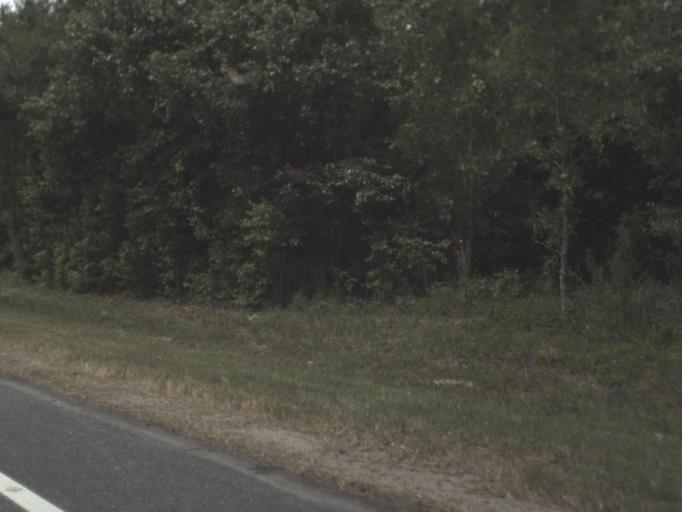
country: US
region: Florida
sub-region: Suwannee County
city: Wellborn
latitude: 30.0812
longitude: -82.9452
